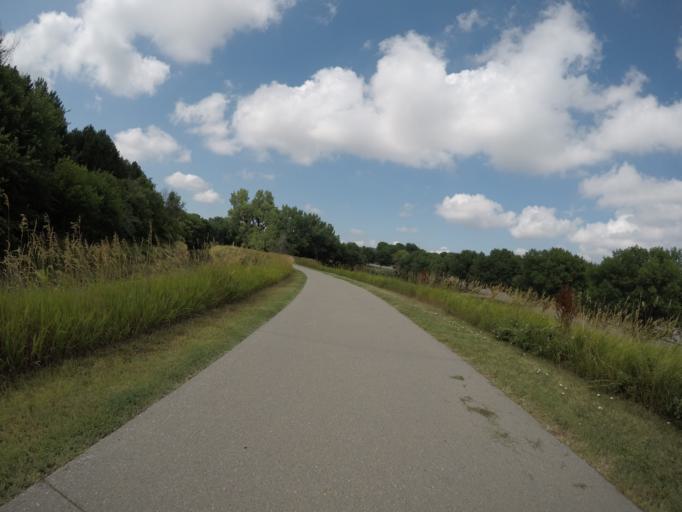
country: US
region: Nebraska
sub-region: Buffalo County
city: Kearney
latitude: 40.7015
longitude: -99.1147
